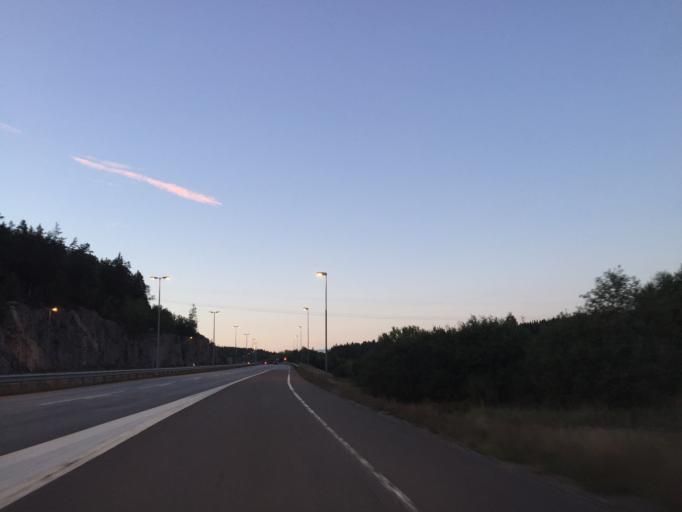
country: NO
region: Akershus
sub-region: Vestby
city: Vestby
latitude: 59.5173
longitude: 10.7257
